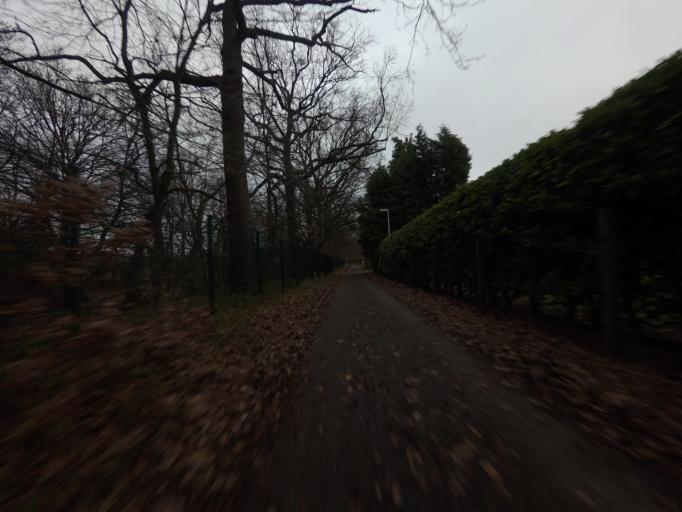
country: BE
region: Flanders
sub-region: Provincie Antwerpen
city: Hoboken
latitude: 51.1613
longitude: 4.3637
